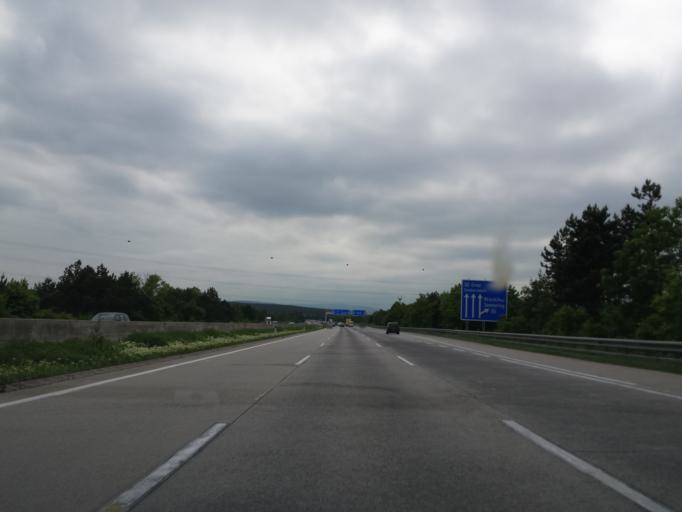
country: AT
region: Lower Austria
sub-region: Politischer Bezirk Neunkirchen
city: Breitenau
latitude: 47.7233
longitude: 16.1420
